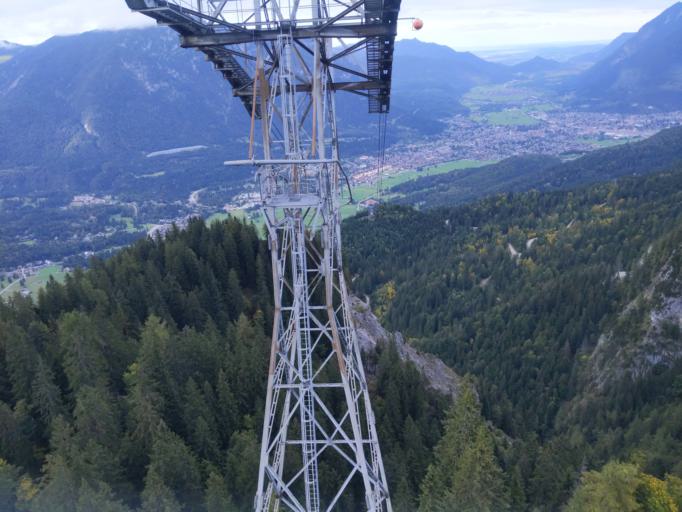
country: DE
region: Bavaria
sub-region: Upper Bavaria
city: Grainau
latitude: 47.4494
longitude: 11.0544
